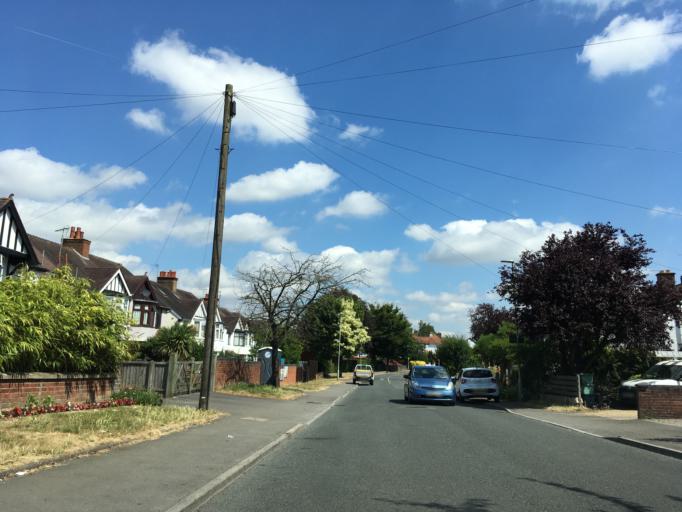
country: GB
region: England
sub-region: Gloucestershire
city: Barnwood
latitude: 51.8736
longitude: -2.2211
